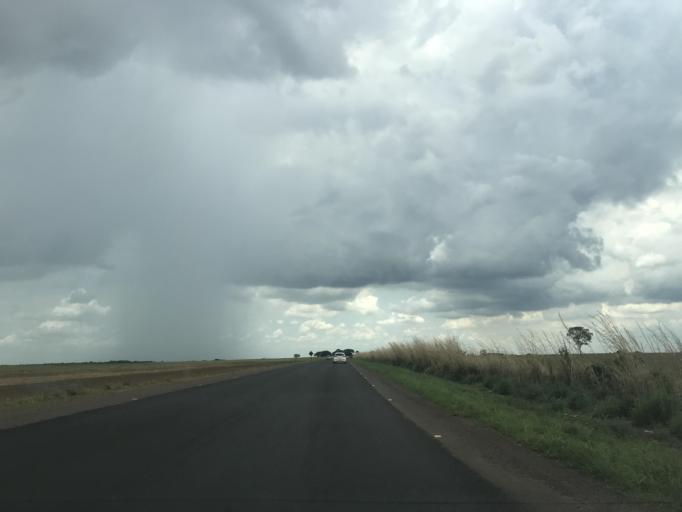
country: BR
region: Goias
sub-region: Vianopolis
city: Vianopolis
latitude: -16.8596
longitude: -48.5416
